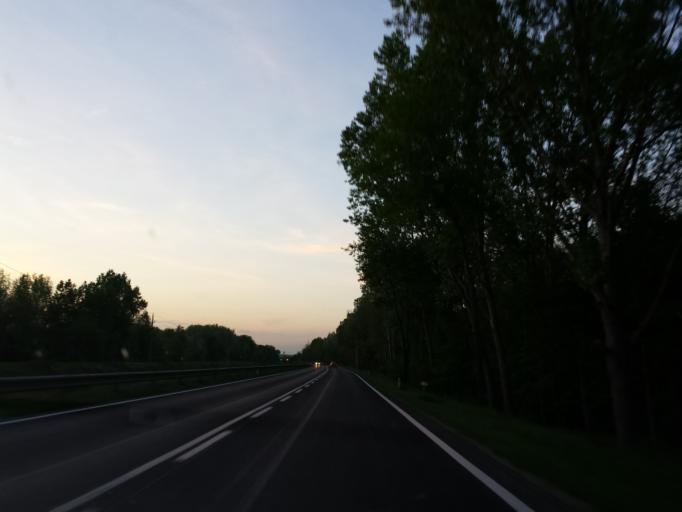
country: AT
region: Lower Austria
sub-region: Politischer Bezirk Tulln
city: Tulln
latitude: 48.3481
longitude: 16.0594
